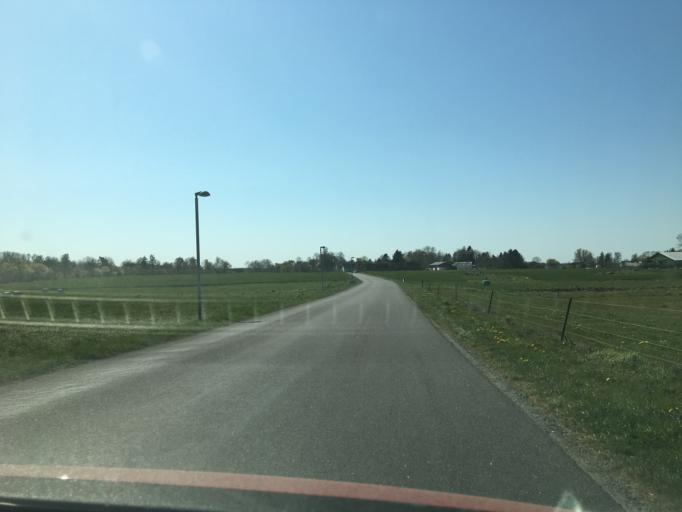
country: DK
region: Zealand
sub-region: Guldborgsund Kommune
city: Nykobing Falster
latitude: 54.7503
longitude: 11.7847
